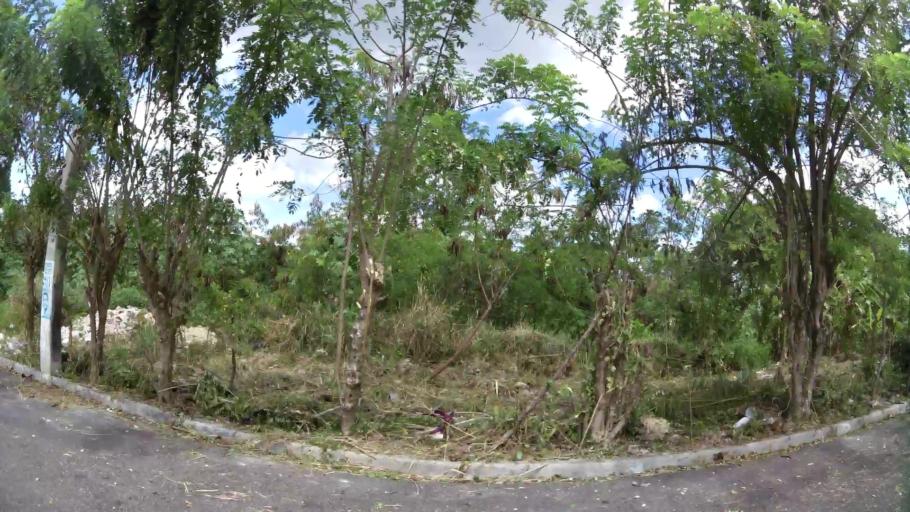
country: DO
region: Nacional
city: Ensanche Luperon
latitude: 18.5253
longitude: -69.9022
